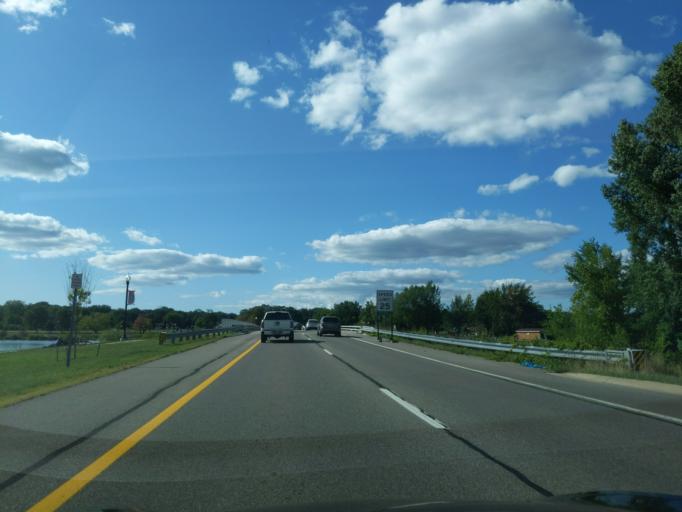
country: US
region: Michigan
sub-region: Muskegon County
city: North Muskegon
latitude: 43.2623
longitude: -86.2444
